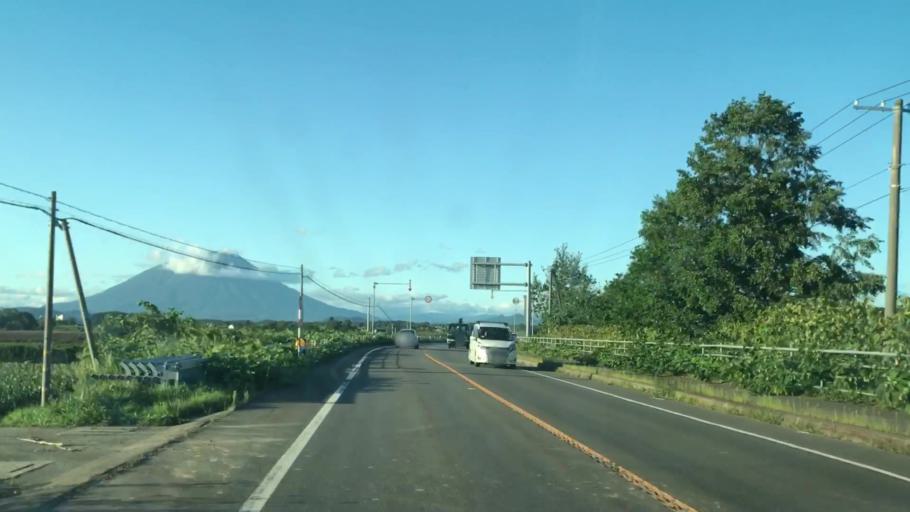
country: JP
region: Hokkaido
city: Date
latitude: 42.6448
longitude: 140.8041
